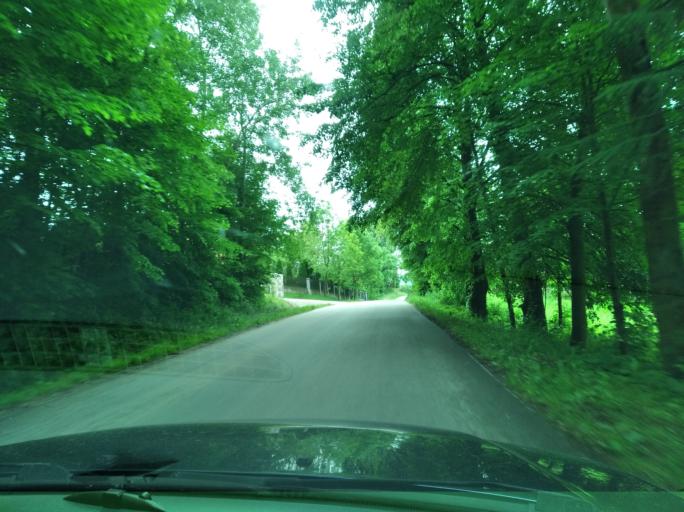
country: PL
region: Subcarpathian Voivodeship
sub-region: Powiat przemyski
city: Dubiecko
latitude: 49.8319
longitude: 22.3948
